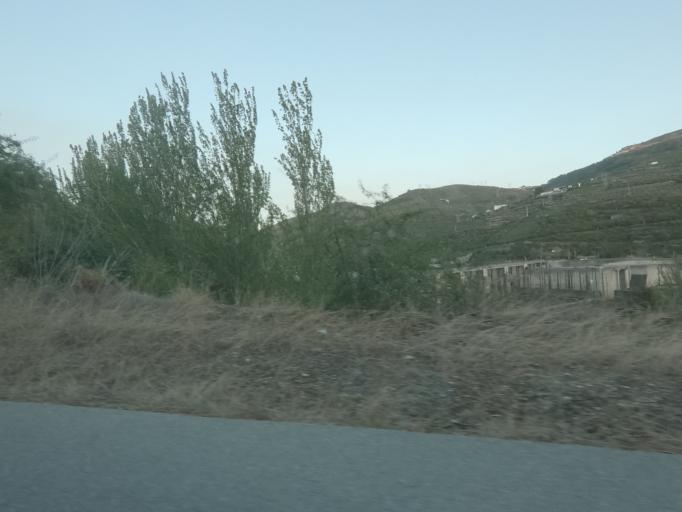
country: PT
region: Vila Real
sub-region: Peso da Regua
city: Peso da Regua
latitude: 41.1489
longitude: -7.7424
